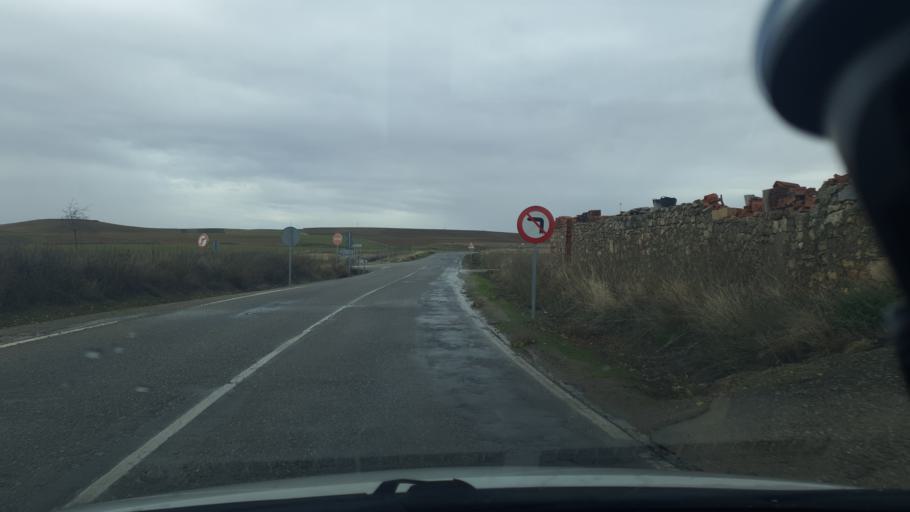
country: ES
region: Castille and Leon
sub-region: Provincia de Segovia
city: Segovia
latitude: 40.9637
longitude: -4.1371
